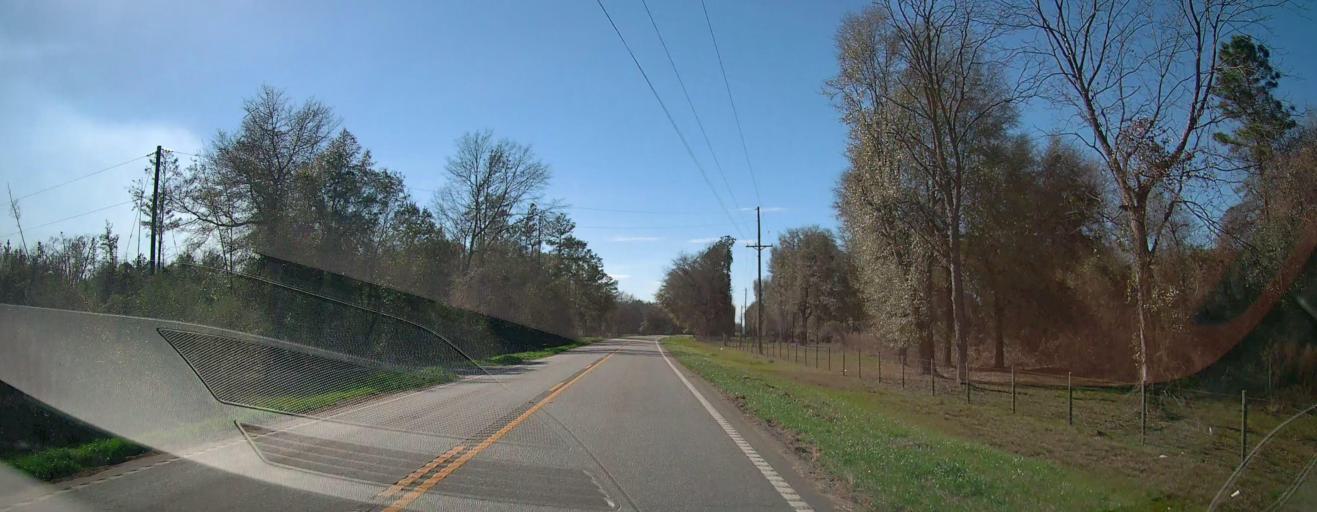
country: US
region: Georgia
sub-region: Macon County
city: Oglethorpe
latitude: 32.3300
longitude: -84.0897
